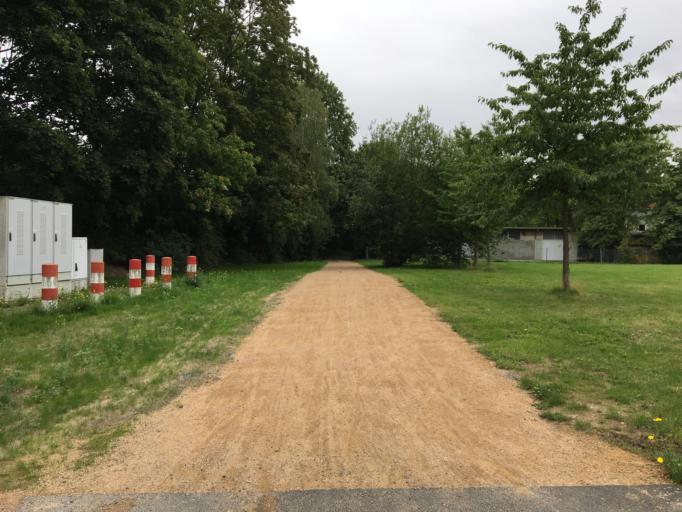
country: DE
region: Lower Saxony
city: Braunschweig
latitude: 52.2771
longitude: 10.5503
